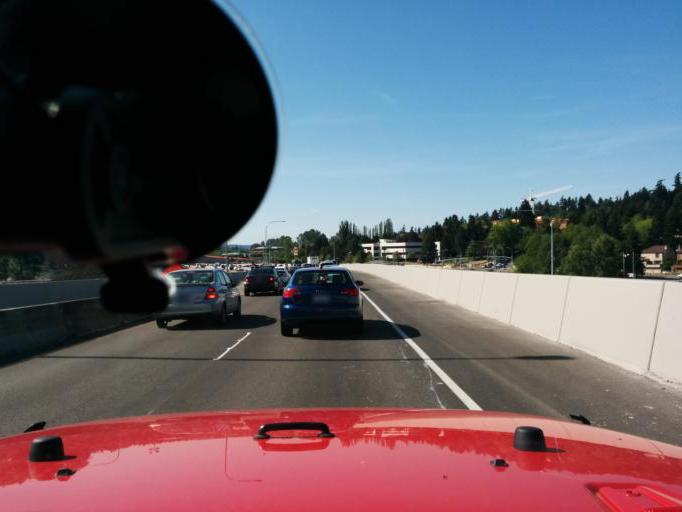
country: US
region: Washington
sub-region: King County
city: Yarrow Point
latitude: 47.6389
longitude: -122.1948
